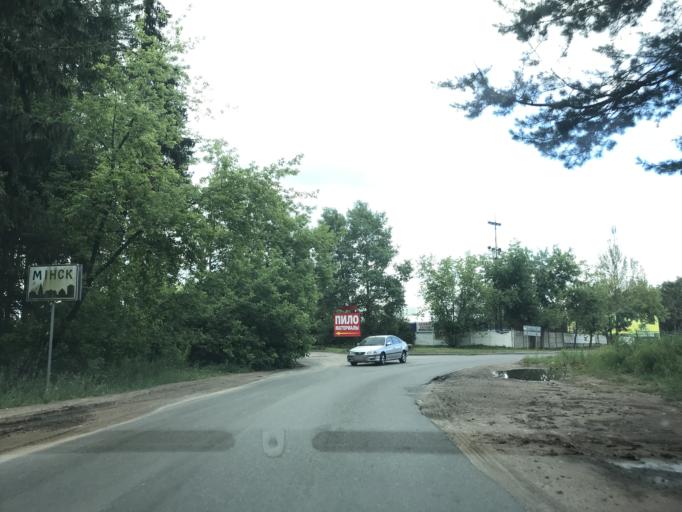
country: BY
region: Minsk
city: Borovlyany
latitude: 53.9592
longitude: 27.6906
